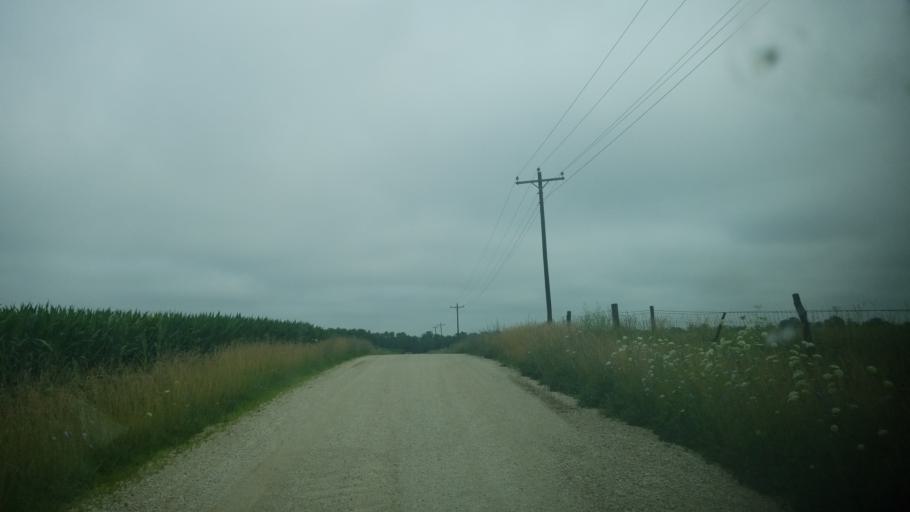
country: US
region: Missouri
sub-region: Pike County
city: Bowling Green
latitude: 39.3522
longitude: -91.2617
